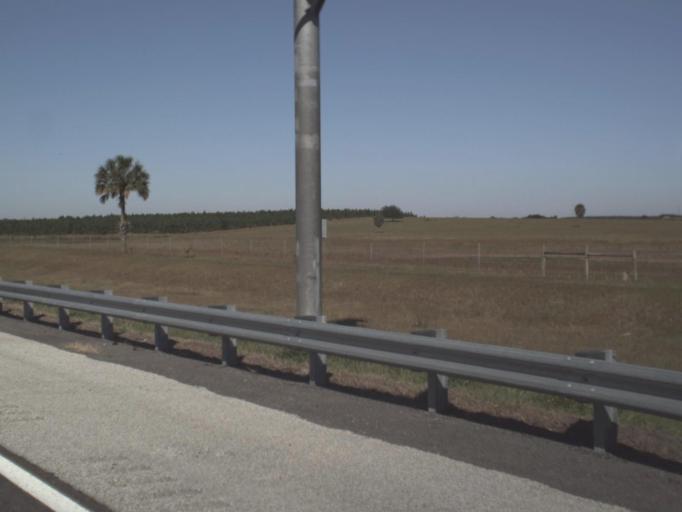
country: US
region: Florida
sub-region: Lake County
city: Yalaha
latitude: 28.6649
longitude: -81.8324
